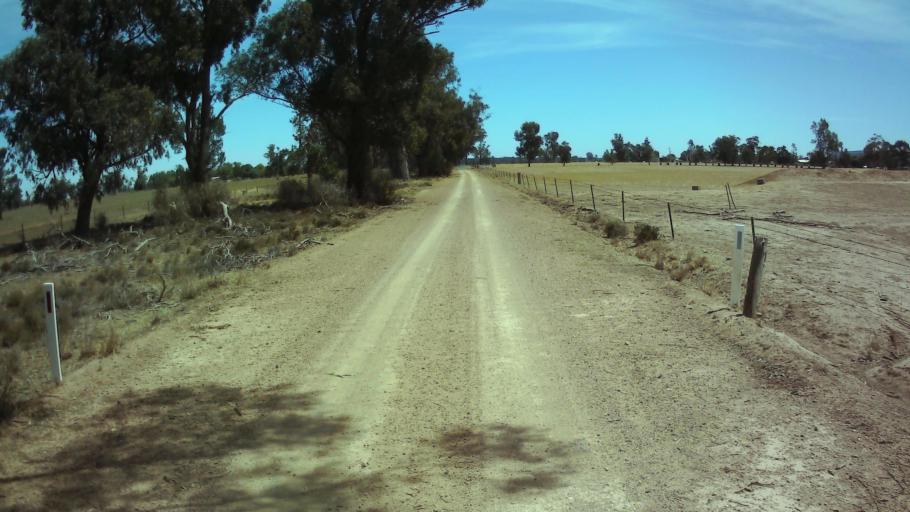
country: AU
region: New South Wales
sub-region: Weddin
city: Grenfell
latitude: -34.0328
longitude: 147.9429
